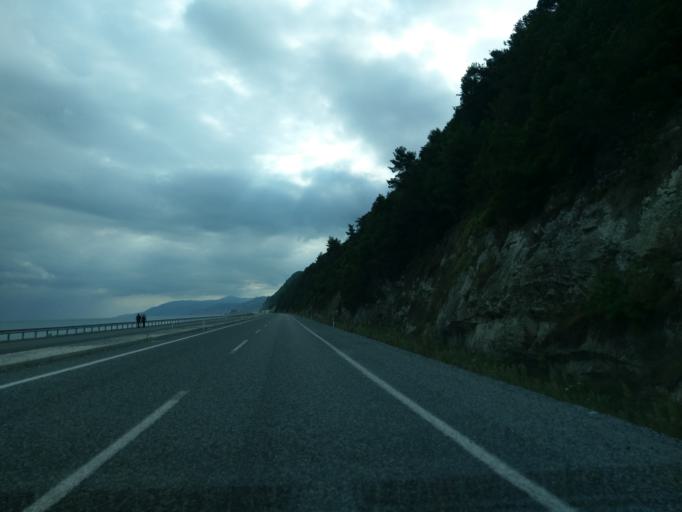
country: TR
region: Kastamonu
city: Catalzeytin
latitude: 41.9489
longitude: 34.2462
